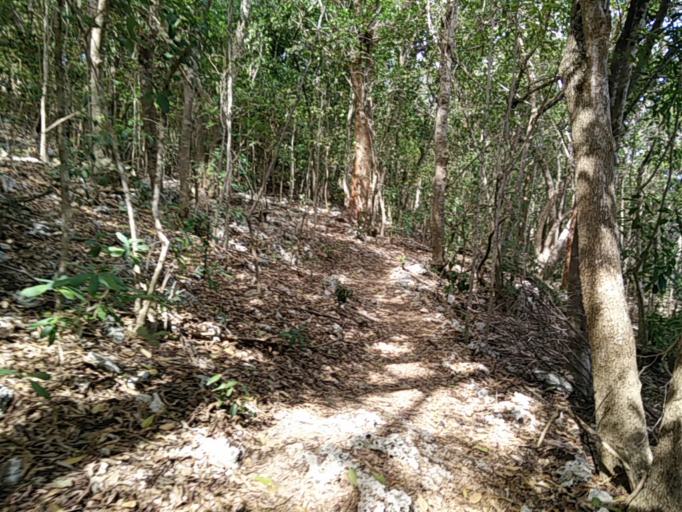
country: GP
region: Guadeloupe
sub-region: Guadeloupe
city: Sainte-Anne
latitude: 16.2107
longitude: -61.4282
